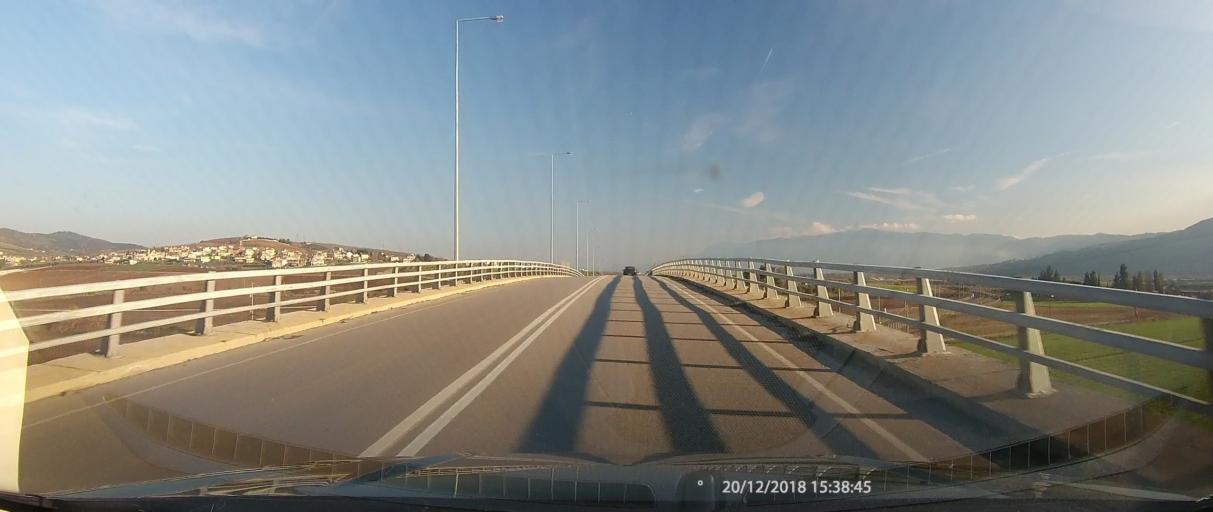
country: GR
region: Central Greece
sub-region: Nomos Fthiotidos
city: Stavros
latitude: 38.9016
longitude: 22.3549
